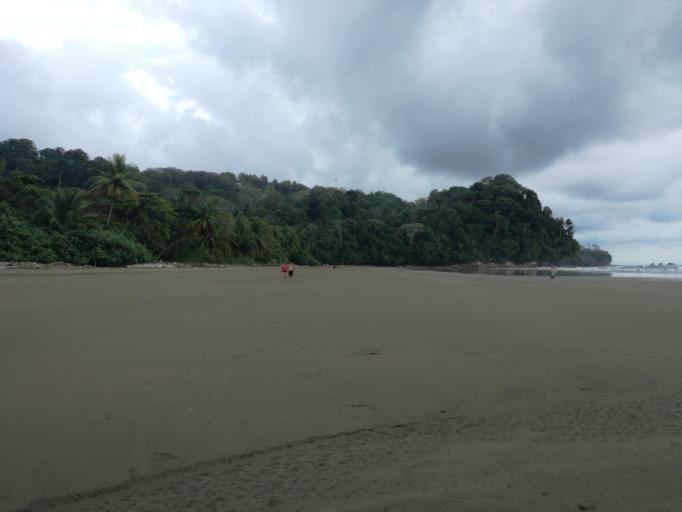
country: CR
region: San Jose
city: Mercedes
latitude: 9.1475
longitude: -83.7310
